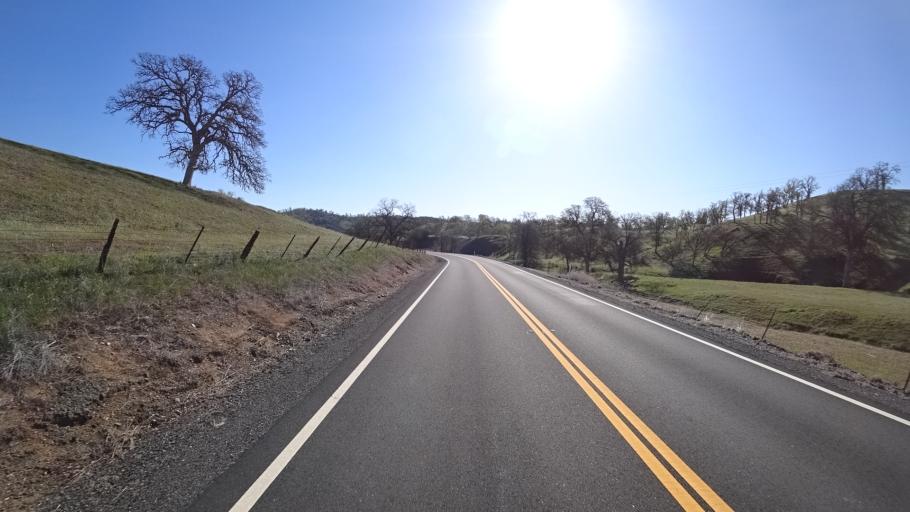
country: US
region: California
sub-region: Glenn County
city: Orland
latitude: 39.6598
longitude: -122.5378
